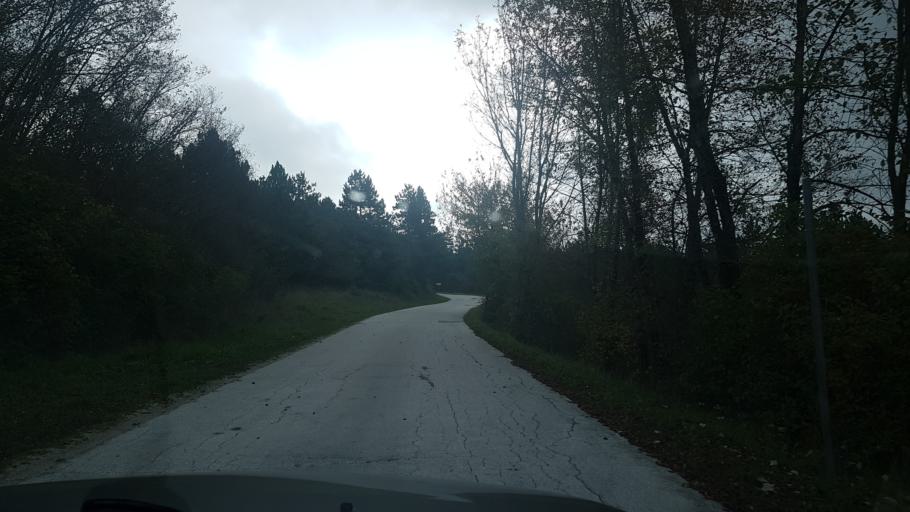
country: HR
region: Istarska
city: Buzet
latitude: 45.5023
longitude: 13.9929
